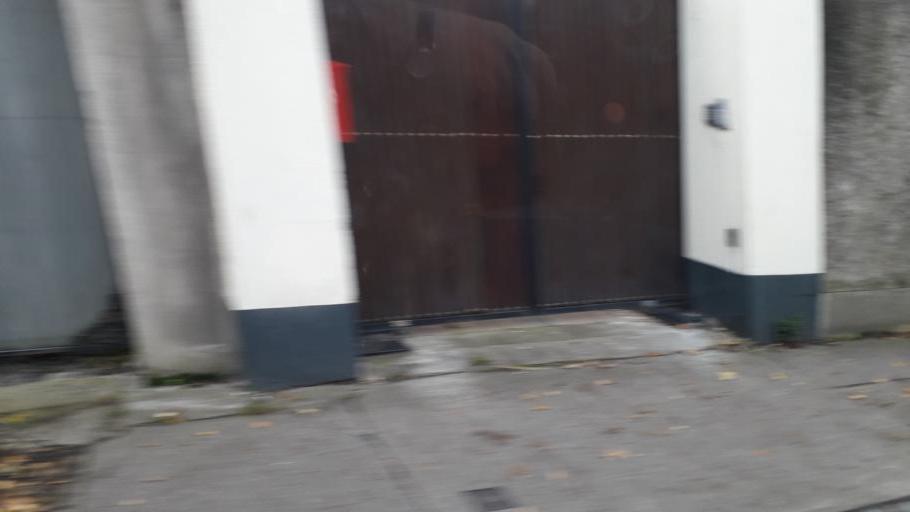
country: IE
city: Milltown
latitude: 53.3169
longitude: -6.2396
